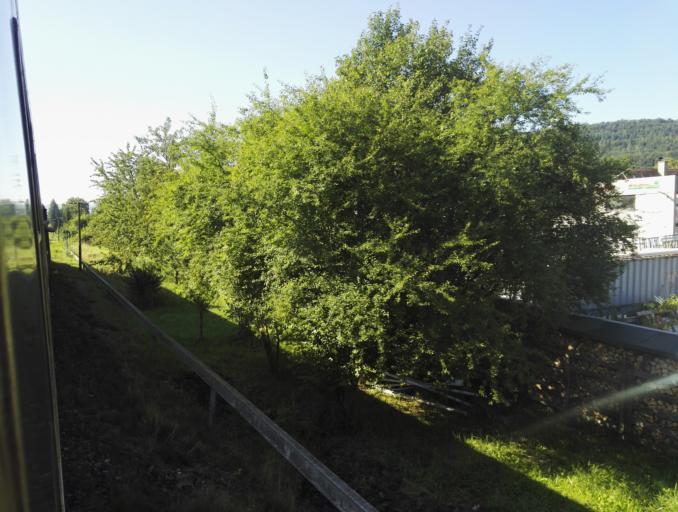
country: DE
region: Baden-Wuerttemberg
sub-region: Regierungsbezirk Stuttgart
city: Rudersberg
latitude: 48.8461
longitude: 9.5381
